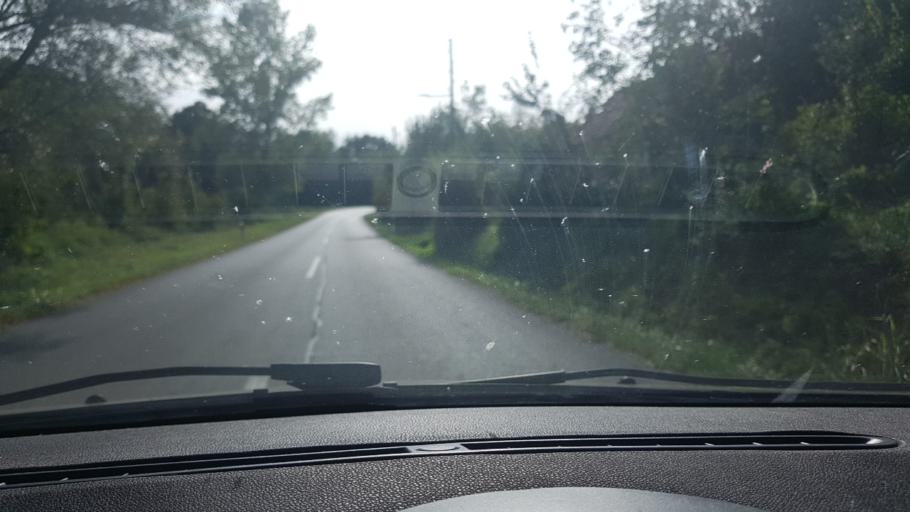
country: HR
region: Krapinsko-Zagorska
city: Zlatar
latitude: 46.1140
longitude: 16.0921
